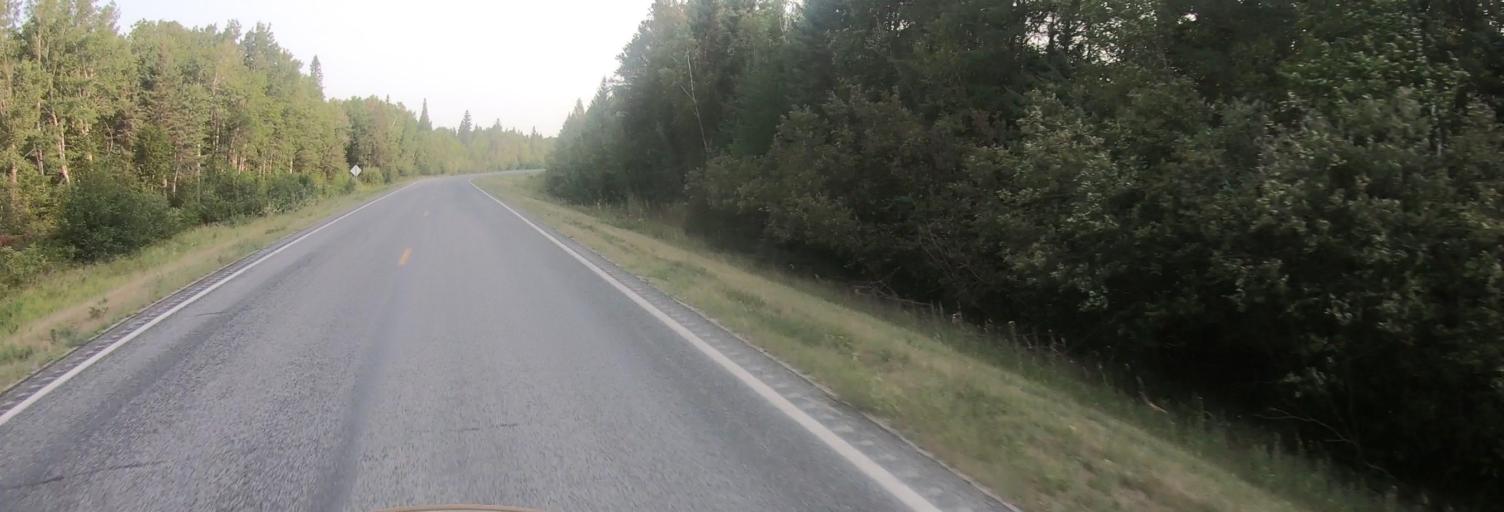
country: US
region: Minnesota
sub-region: Roseau County
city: Warroad
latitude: 48.7395
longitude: -95.3309
